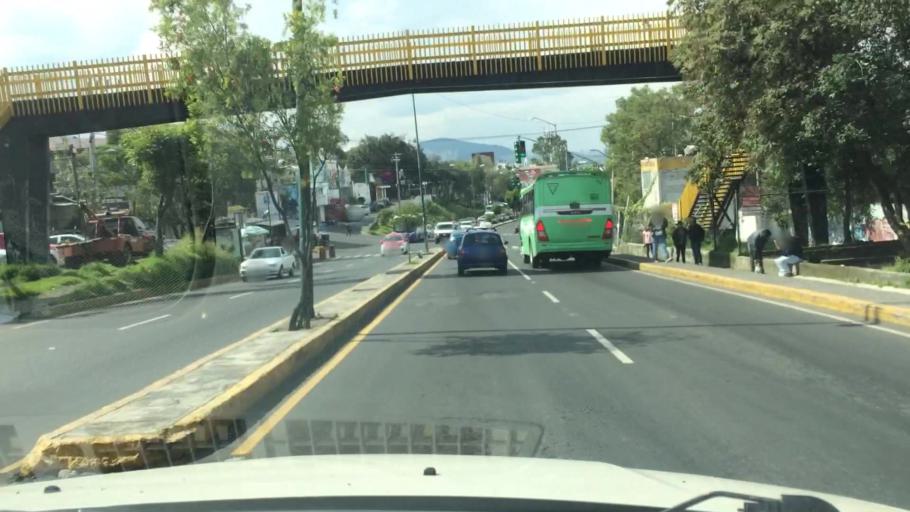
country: MX
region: Mexico City
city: Magdalena Contreras
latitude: 19.2833
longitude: -99.2171
